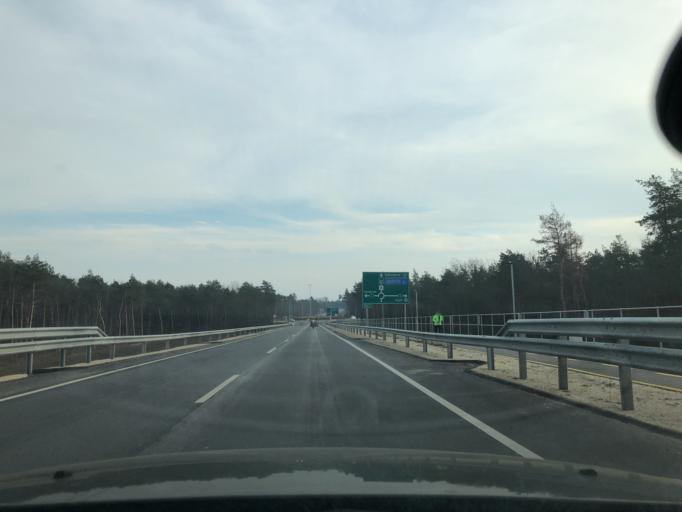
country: HU
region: Gyor-Moson-Sopron
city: Gyor
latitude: 47.7260
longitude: 17.7023
